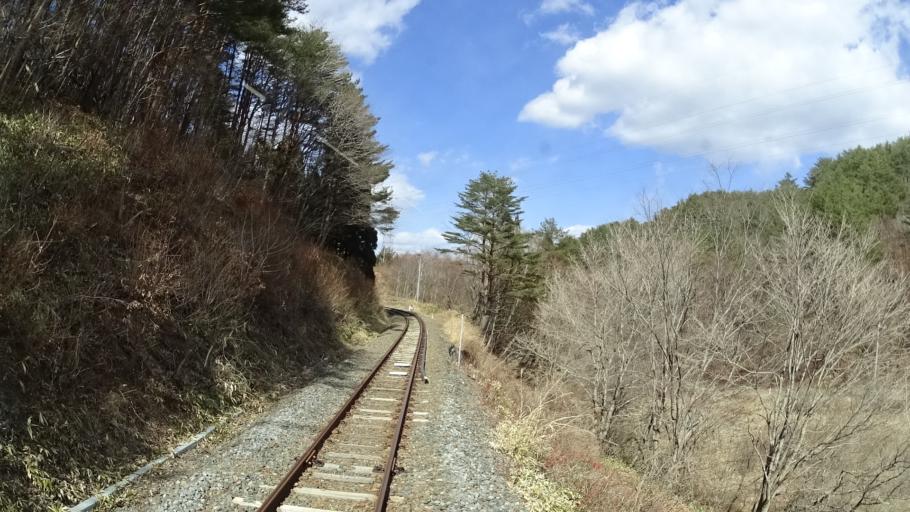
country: JP
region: Iwate
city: Yamada
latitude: 39.4983
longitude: 141.9296
